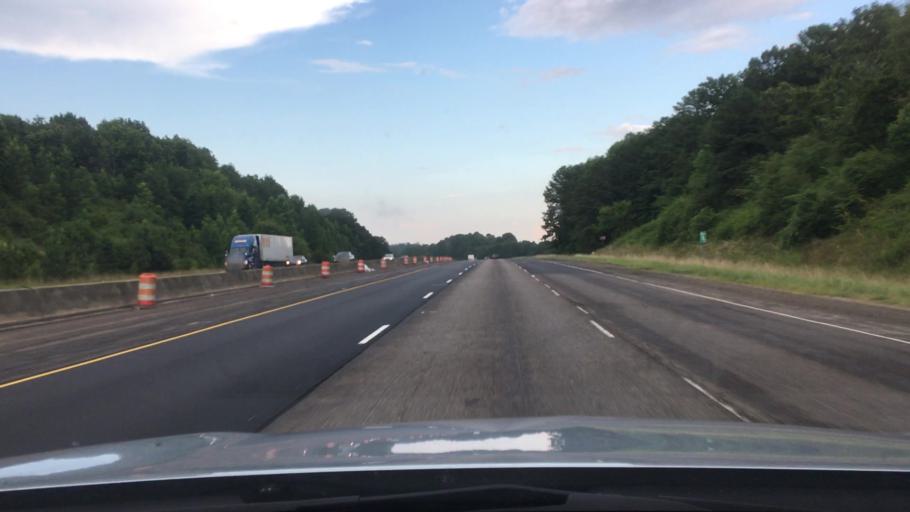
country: US
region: Alabama
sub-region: Shelby County
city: Helena
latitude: 33.3414
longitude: -86.8932
